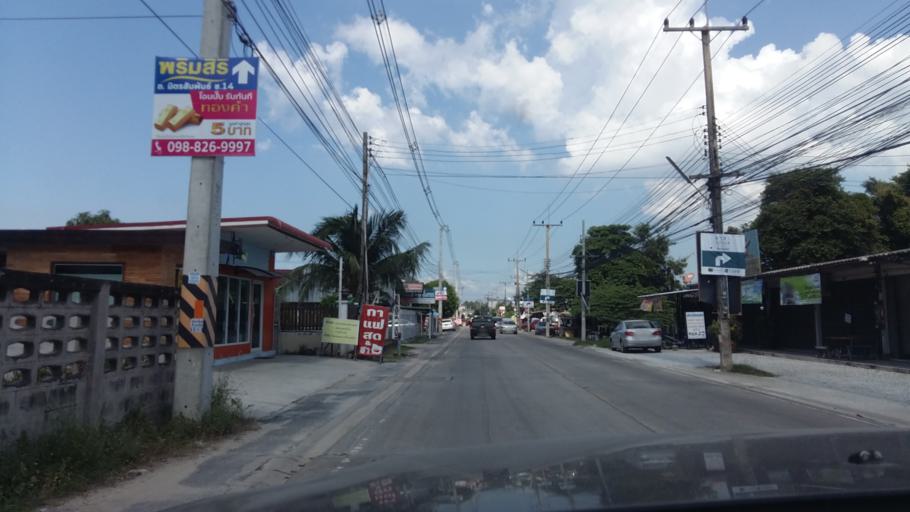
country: TH
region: Chon Buri
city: Chon Buri
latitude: 13.3075
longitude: 100.9313
